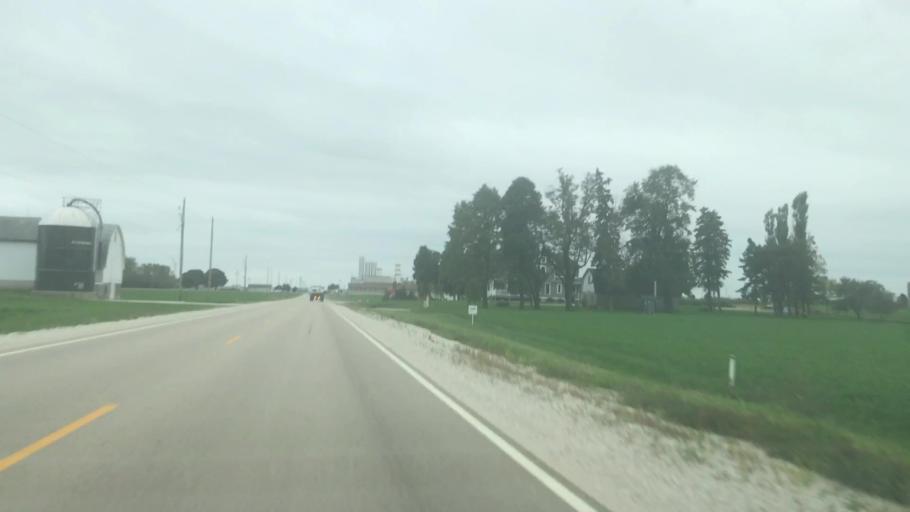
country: US
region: Wisconsin
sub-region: Fond du Lac County
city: Oakfield
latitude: 43.6217
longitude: -88.5417
